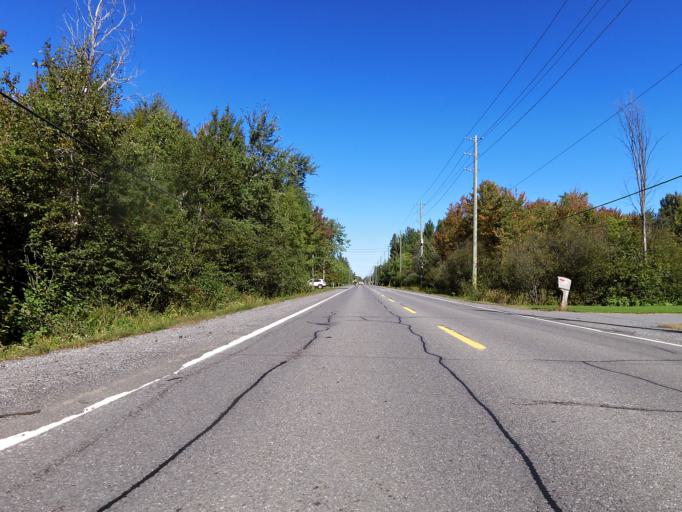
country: CA
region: Ontario
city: Clarence-Rockland
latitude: 45.3611
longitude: -75.4518
